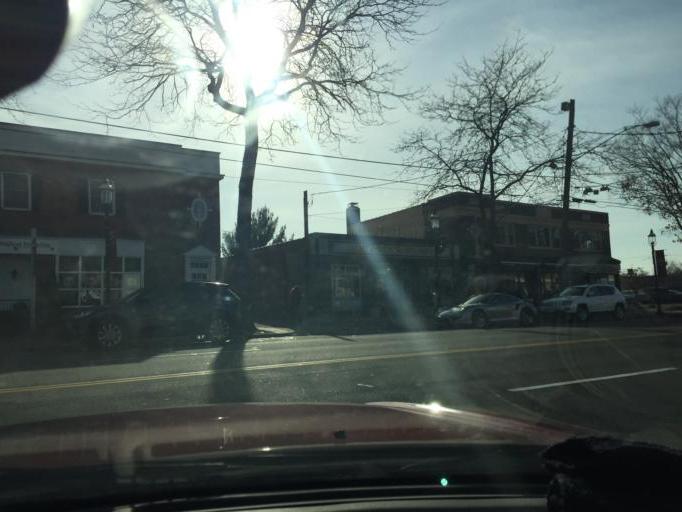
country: US
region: Connecticut
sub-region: Fairfield County
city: Fairfield
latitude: 41.1411
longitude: -73.2594
